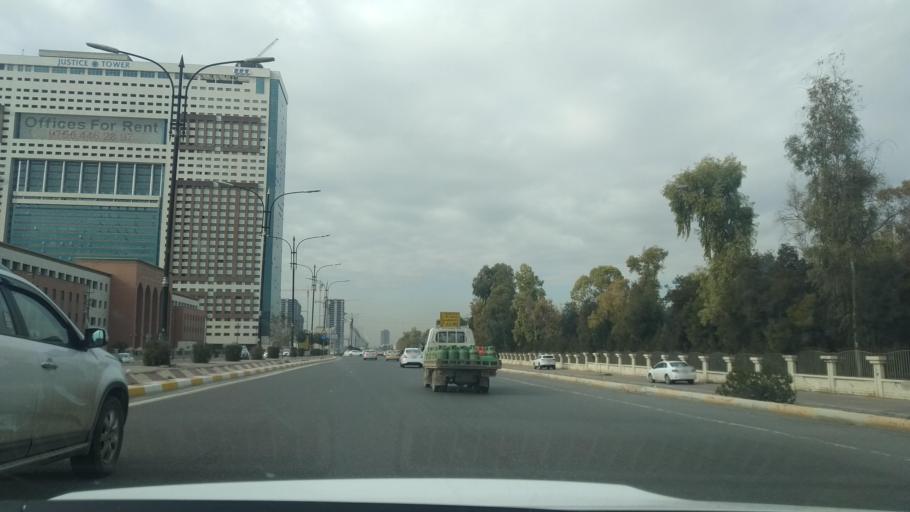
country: IQ
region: Arbil
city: Erbil
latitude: 36.1835
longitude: 43.9817
